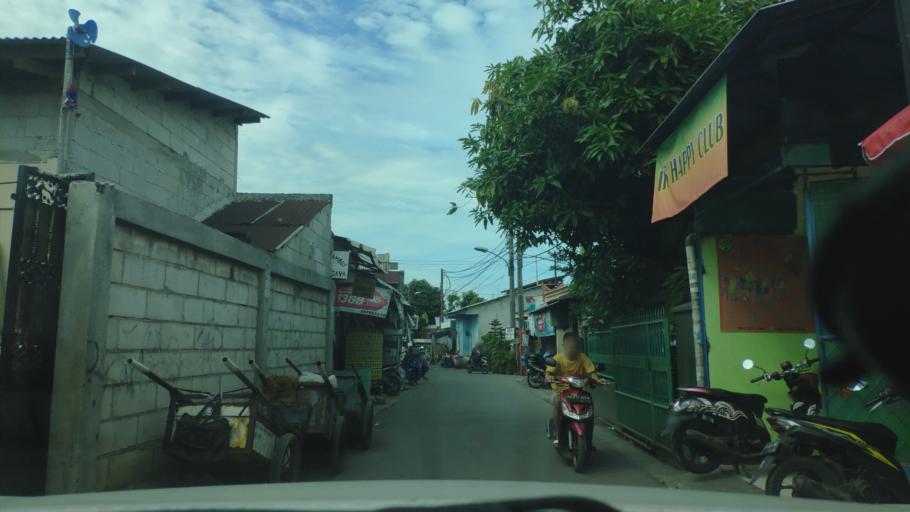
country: ID
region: West Java
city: Ciputat
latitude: -6.2212
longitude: 106.7134
